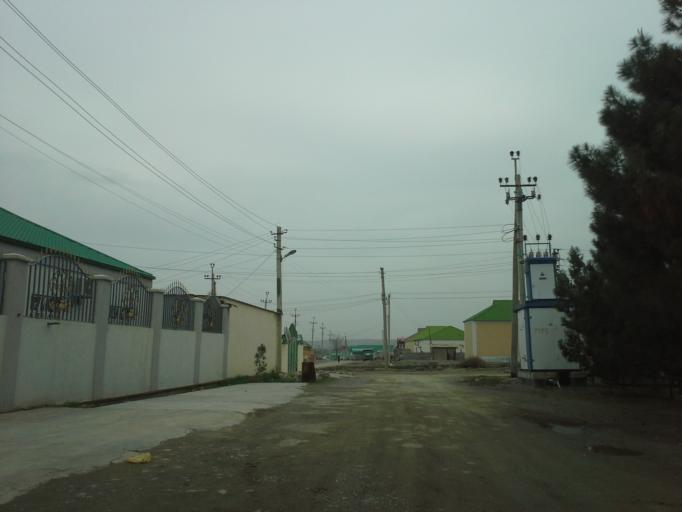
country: TM
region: Ahal
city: Abadan
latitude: 37.9817
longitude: 58.2188
